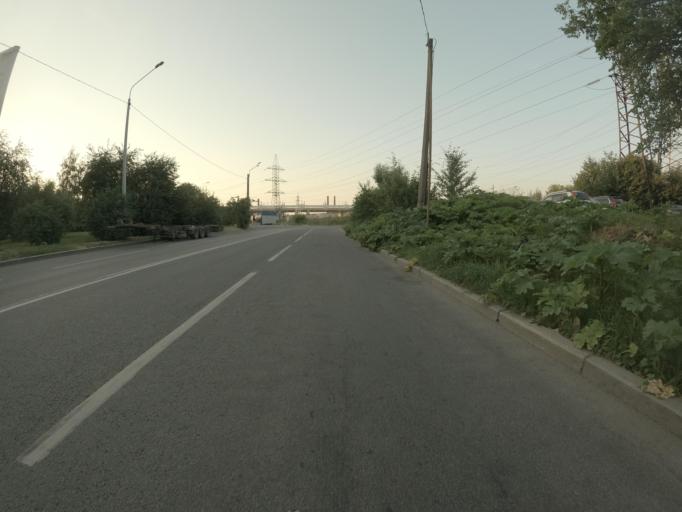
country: RU
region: St.-Petersburg
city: Avtovo
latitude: 59.8787
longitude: 30.2795
